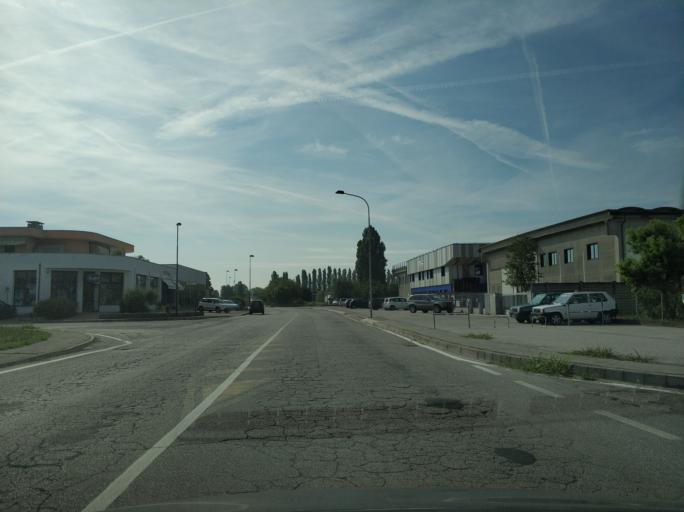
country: IT
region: Veneto
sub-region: Provincia di Padova
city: Este
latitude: 45.2171
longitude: 11.6751
